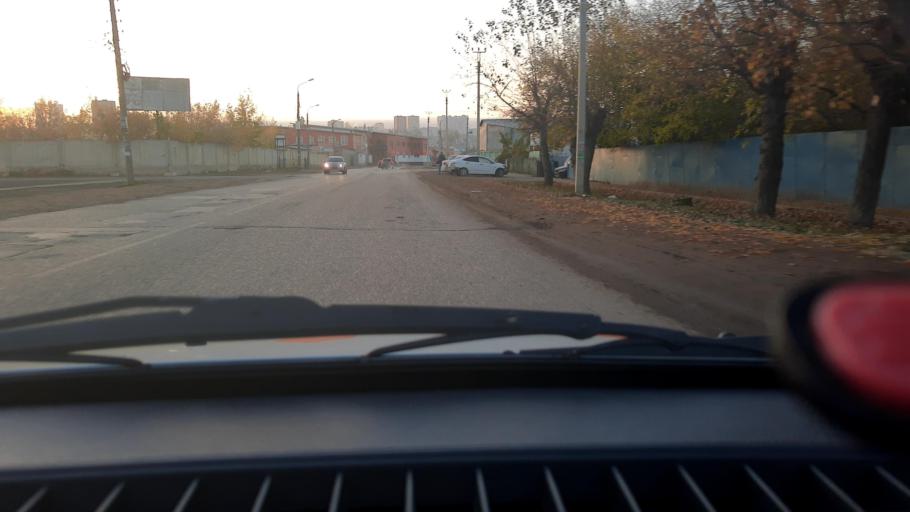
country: RU
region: Bashkortostan
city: Ufa
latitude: 54.7478
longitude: 55.9110
